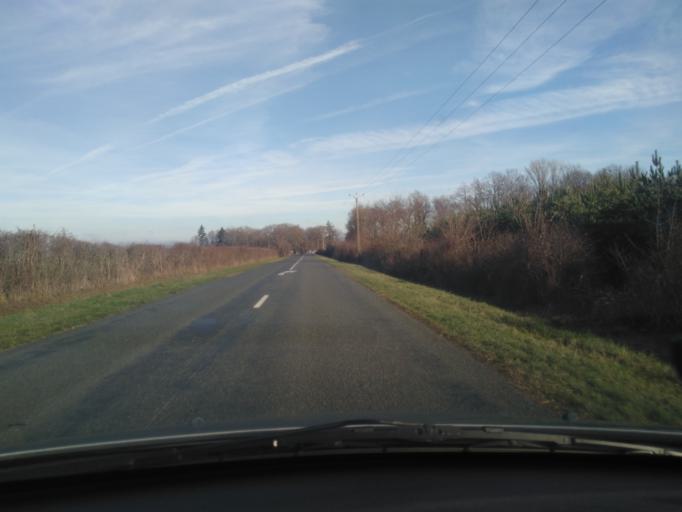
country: FR
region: Centre
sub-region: Departement du Cher
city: Orval
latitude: 46.6687
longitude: 2.4531
